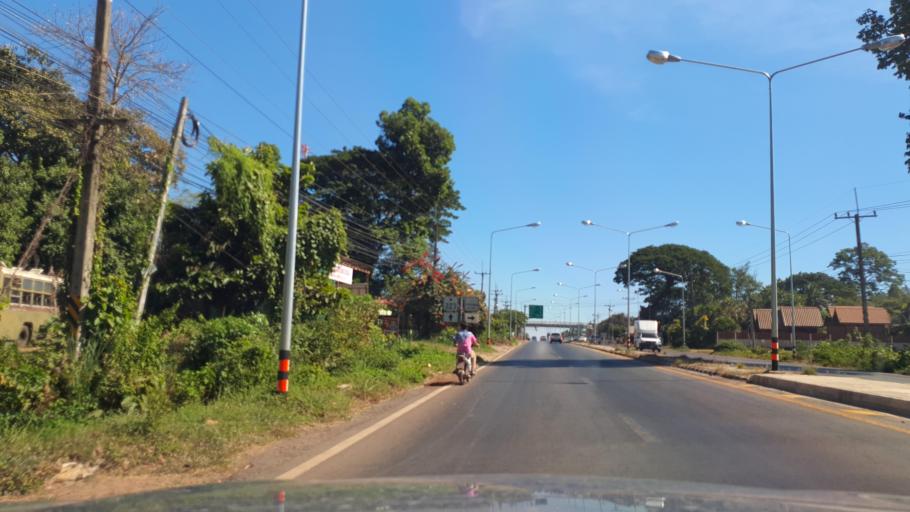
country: TH
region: Sakon Nakhon
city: Sakon Nakhon
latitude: 17.0845
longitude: 104.1881
